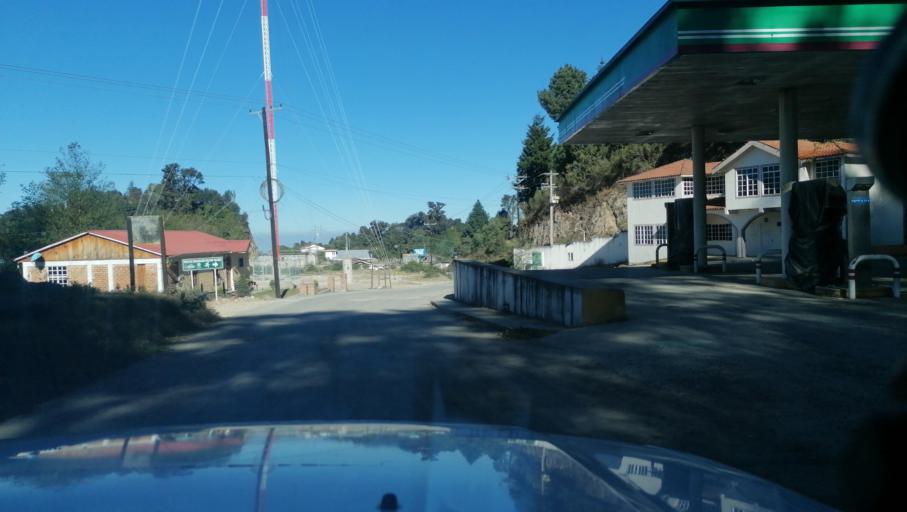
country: MX
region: Chiapas
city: Motozintla de Mendoza
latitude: 15.2622
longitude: -92.2154
